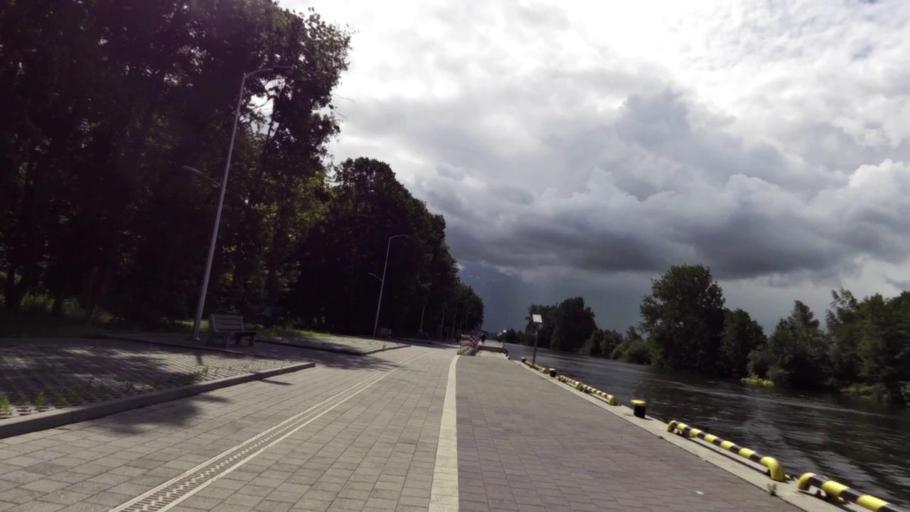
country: PL
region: West Pomeranian Voivodeship
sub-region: Powiat slawienski
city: Darlowo
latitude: 54.4319
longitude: 16.3917
